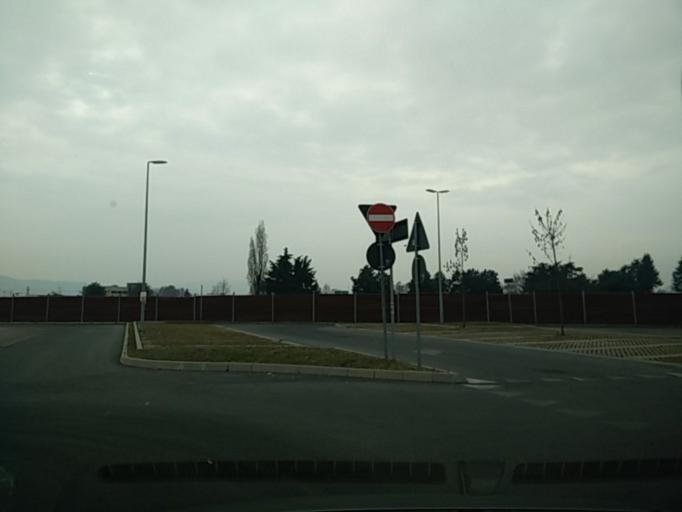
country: IT
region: Piedmont
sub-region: Provincia di Torino
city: Settimo Torinese
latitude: 45.1369
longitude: 7.7338
